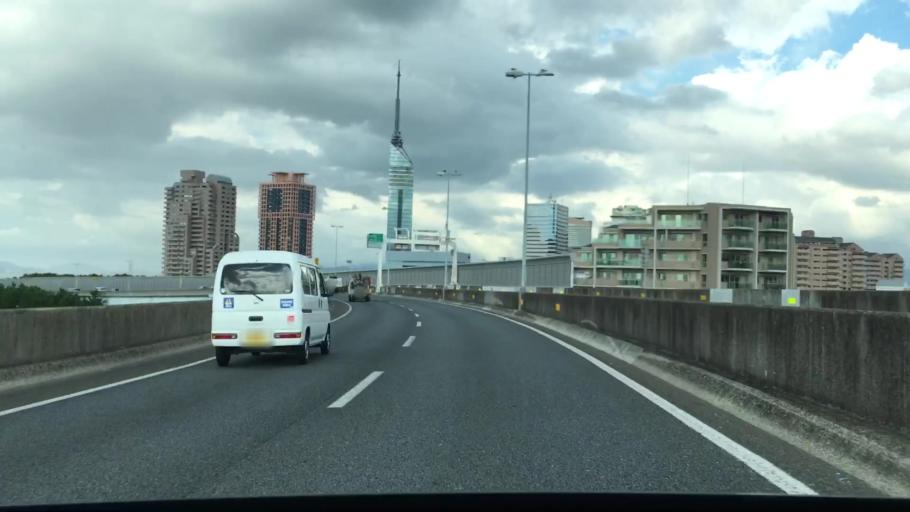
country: JP
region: Fukuoka
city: Fukuoka-shi
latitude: 33.5887
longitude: 130.3436
